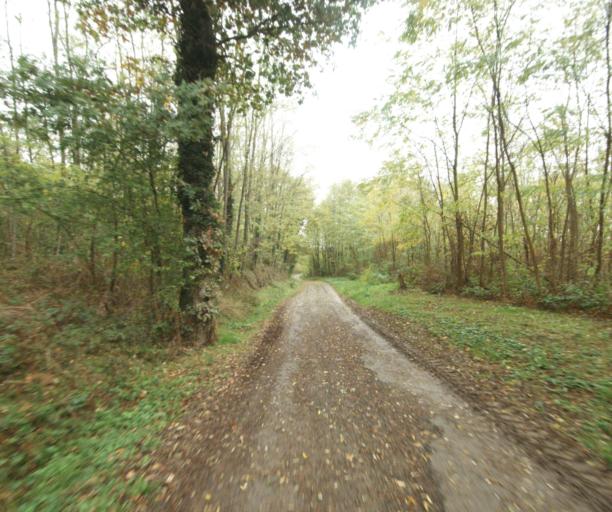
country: FR
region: Bourgogne
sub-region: Departement de Saone-et-Loire
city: Tournus
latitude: 46.4885
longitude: 4.8452
